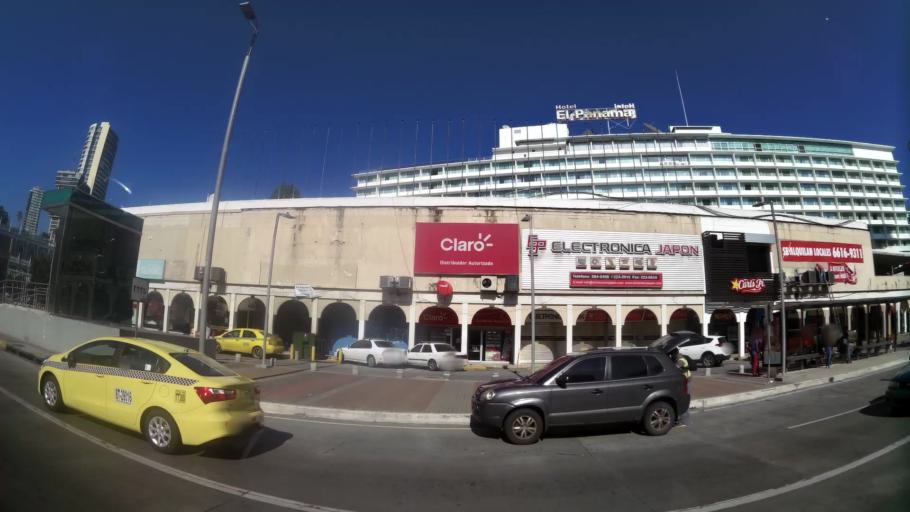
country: PA
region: Panama
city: Panama
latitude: 8.9822
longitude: -79.5272
